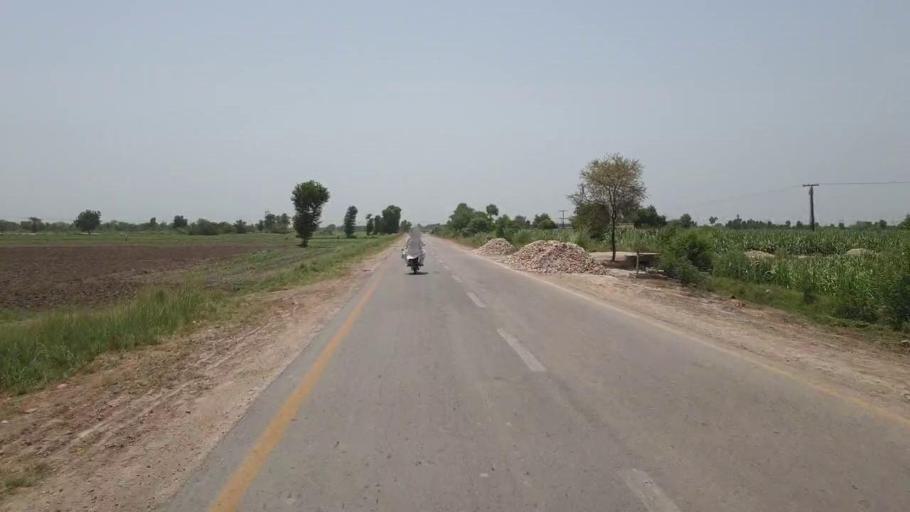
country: PK
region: Sindh
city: Moro
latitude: 26.6086
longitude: 68.0457
